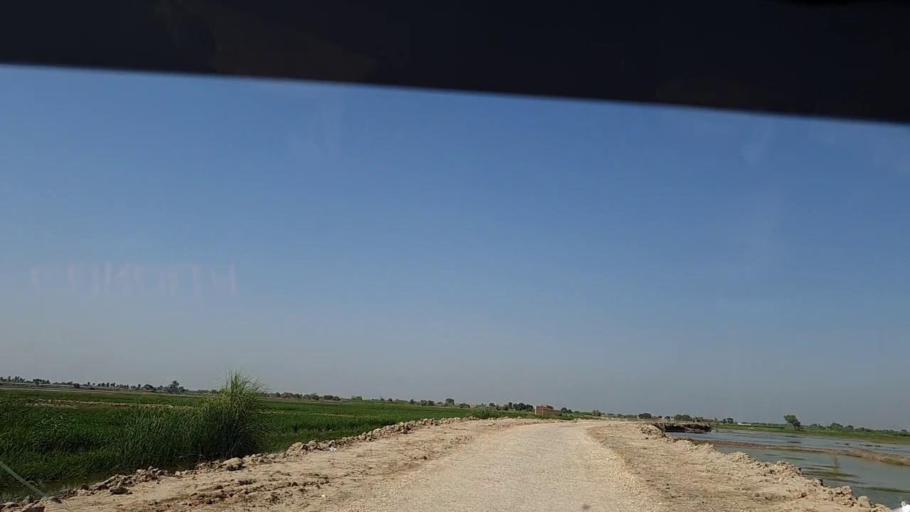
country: PK
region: Sindh
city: Tangwani
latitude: 28.3170
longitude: 69.0829
